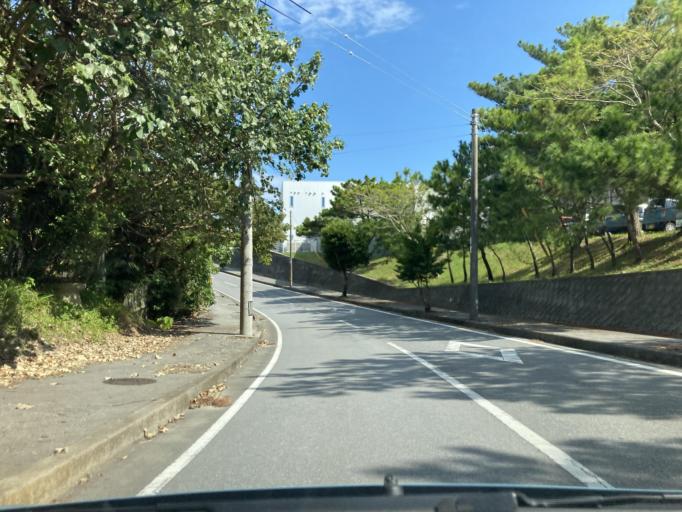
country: JP
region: Okinawa
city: Ginowan
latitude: 26.2429
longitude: 127.7585
